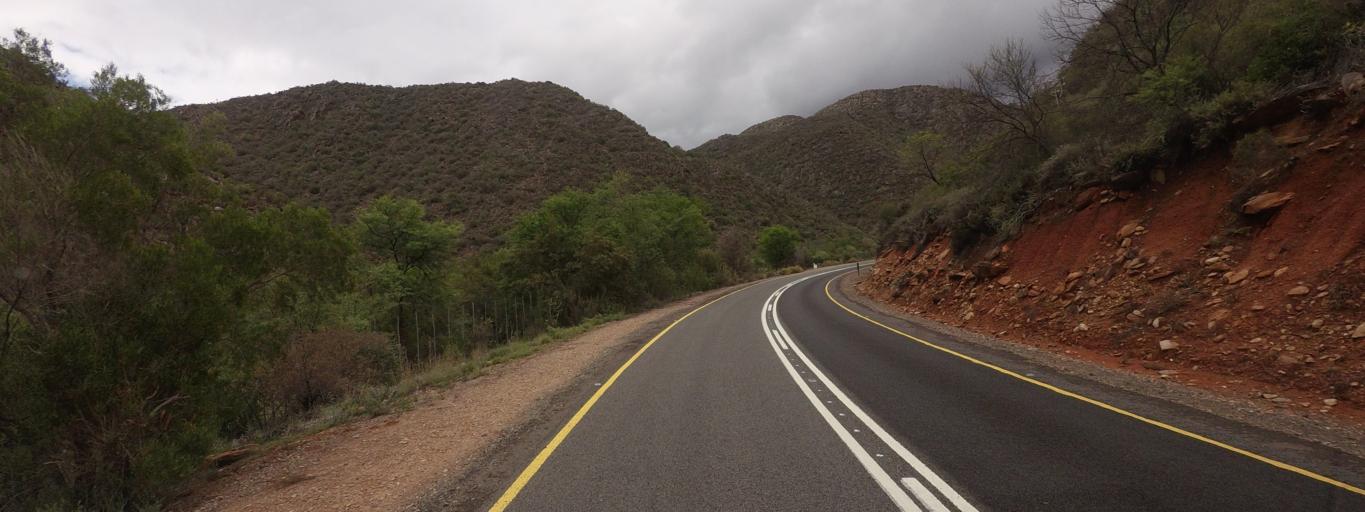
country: ZA
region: Western Cape
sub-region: Eden District Municipality
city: Oudtshoorn
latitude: -33.4471
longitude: 22.2493
